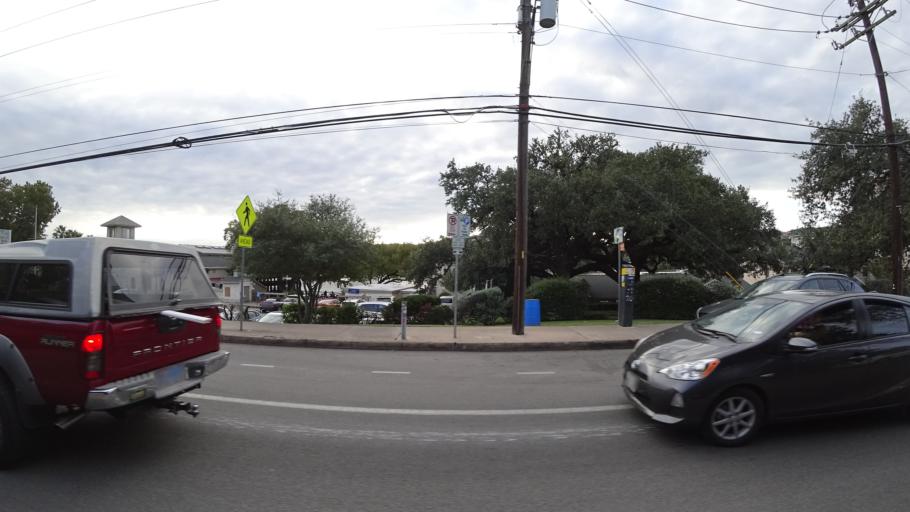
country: US
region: Texas
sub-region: Travis County
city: West Lake Hills
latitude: 30.2957
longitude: -97.7837
